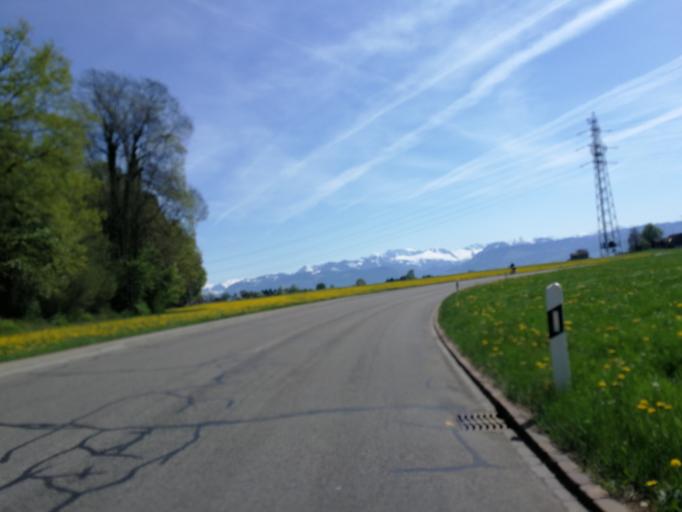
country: CH
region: Zurich
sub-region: Bezirk Hinwil
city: Hinwil
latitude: 47.2911
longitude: 8.8233
